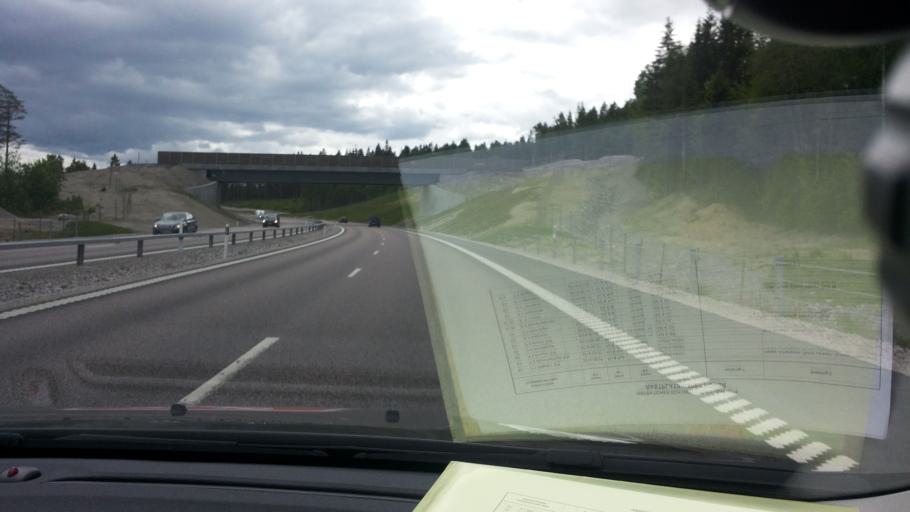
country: SE
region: Vaesternorrland
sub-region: Sundsvalls Kommun
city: Stockvik
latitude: 62.3213
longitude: 17.3401
